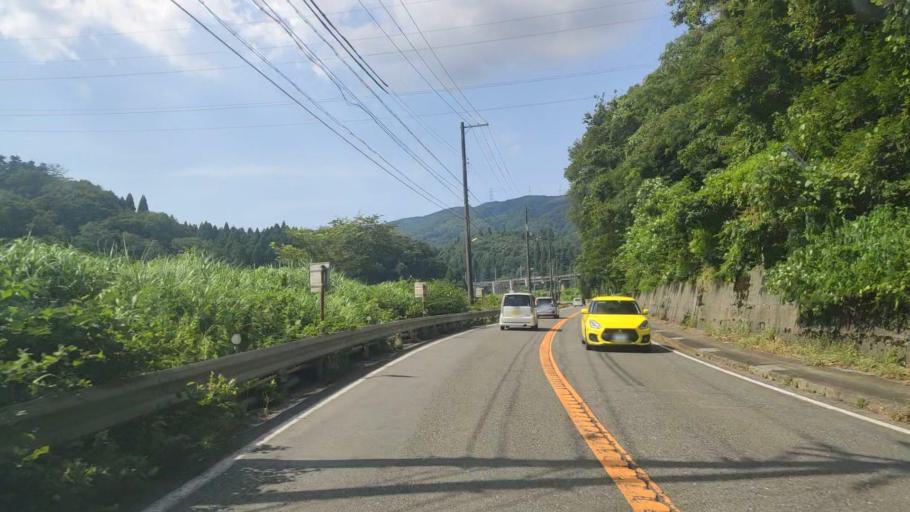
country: JP
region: Fukui
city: Tsuruga
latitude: 35.5471
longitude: 136.1477
